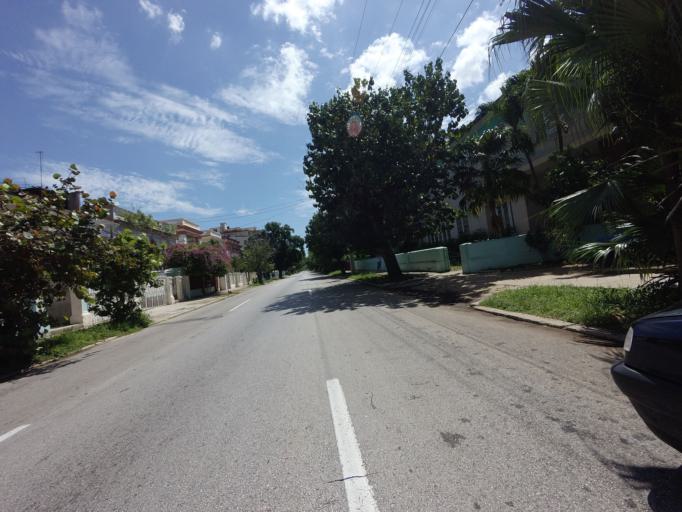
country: CU
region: La Habana
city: Havana
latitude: 23.1355
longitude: -82.4037
